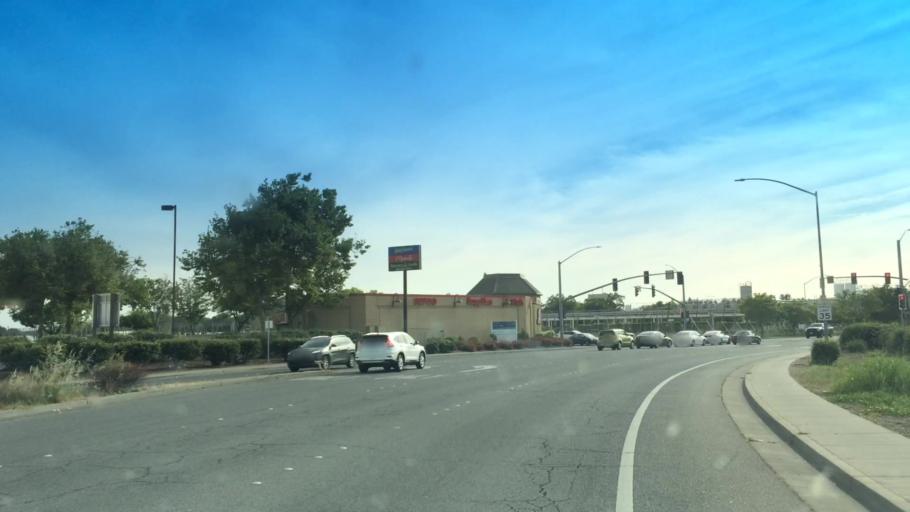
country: US
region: California
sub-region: Butte County
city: Chico
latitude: 39.7252
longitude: -121.8111
